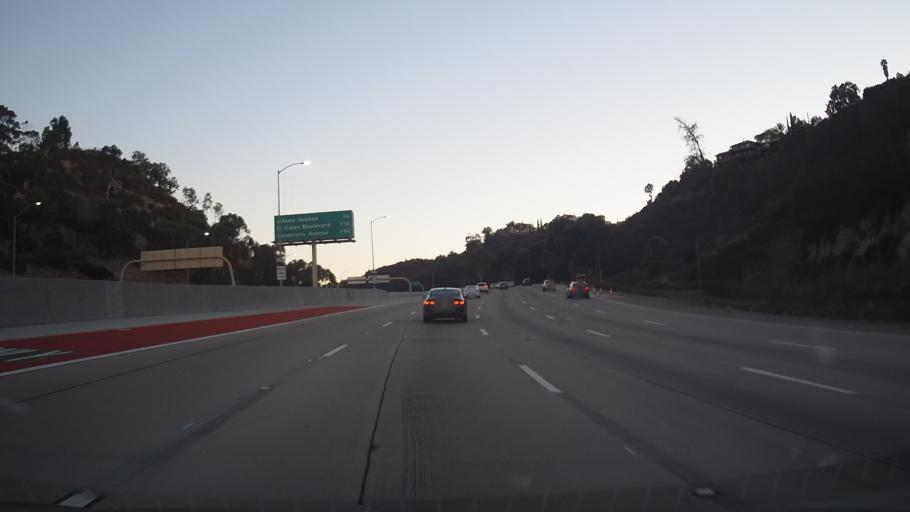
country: US
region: California
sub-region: San Diego County
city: San Diego
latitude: 32.7751
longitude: -117.1128
